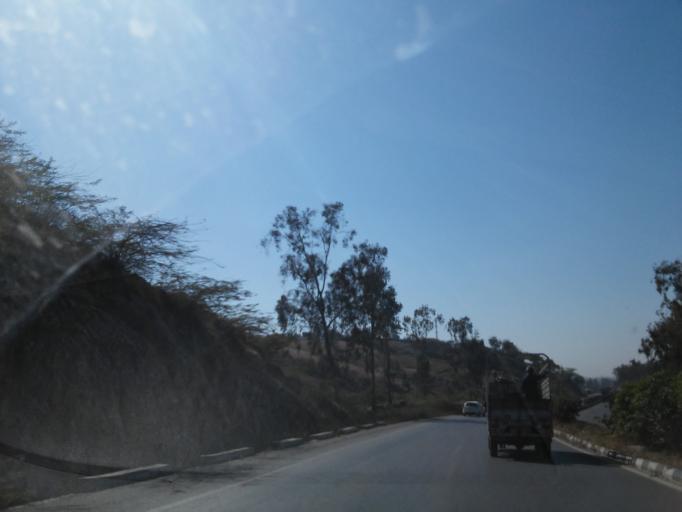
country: IN
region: Rajasthan
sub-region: Dungarpur
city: Dungarpur
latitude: 23.9006
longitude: 73.5454
